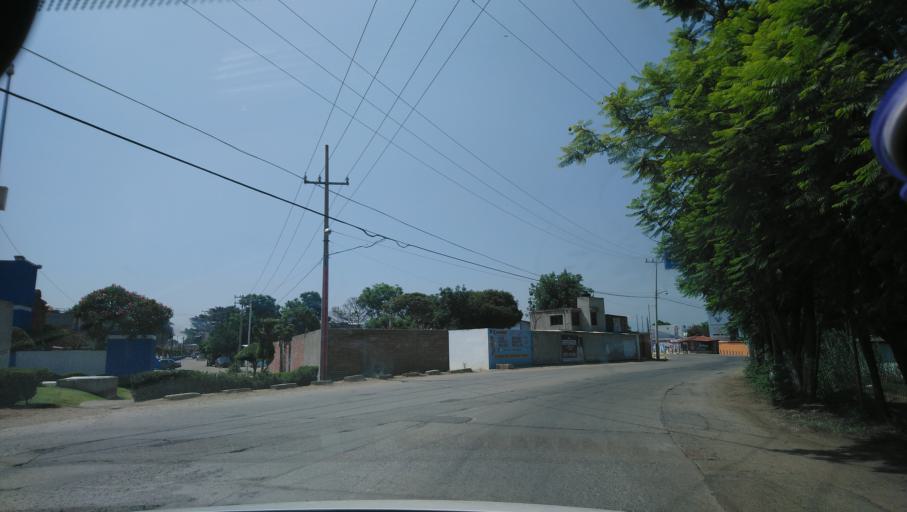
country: MX
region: Oaxaca
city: Santa Maria del Tule
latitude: 17.0472
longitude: -96.6391
